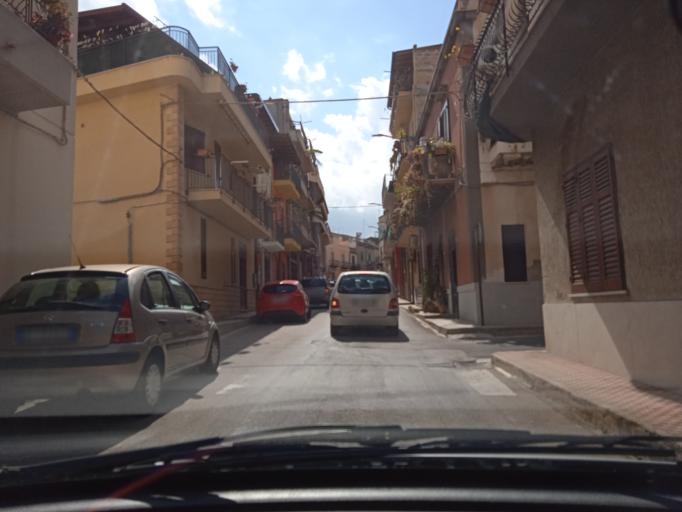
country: IT
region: Sicily
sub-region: Palermo
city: Casteldaccia
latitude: 38.0562
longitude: 13.5326
